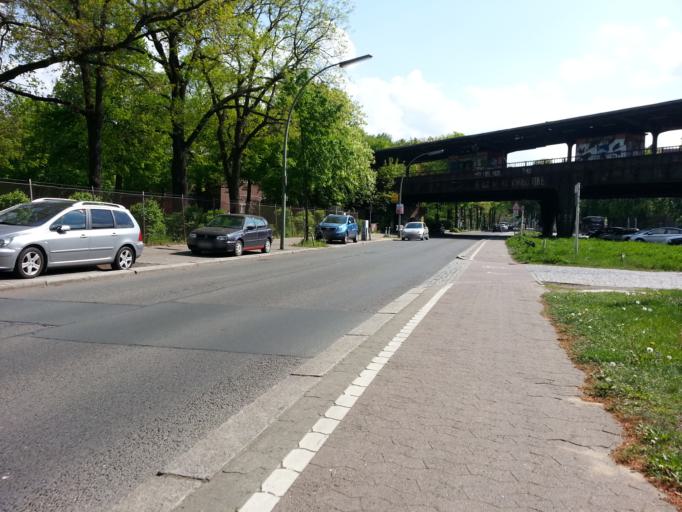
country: DE
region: Berlin
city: Siemensstadt
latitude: 52.5398
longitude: 13.2632
